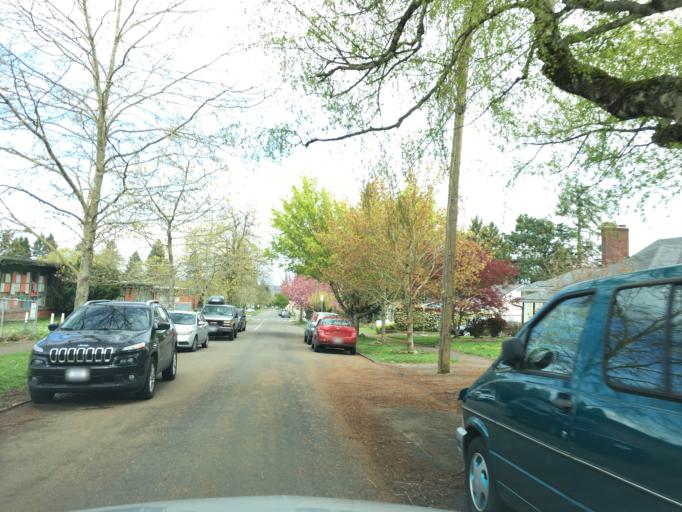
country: US
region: Oregon
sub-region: Multnomah County
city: Lents
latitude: 45.5541
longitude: -122.5932
